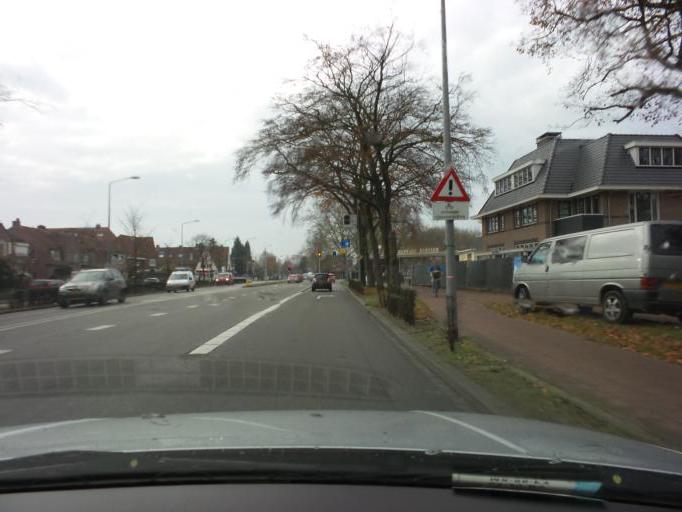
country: NL
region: North Holland
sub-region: Gemeente Hilversum
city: Hilversum
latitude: 52.2372
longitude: 5.1956
